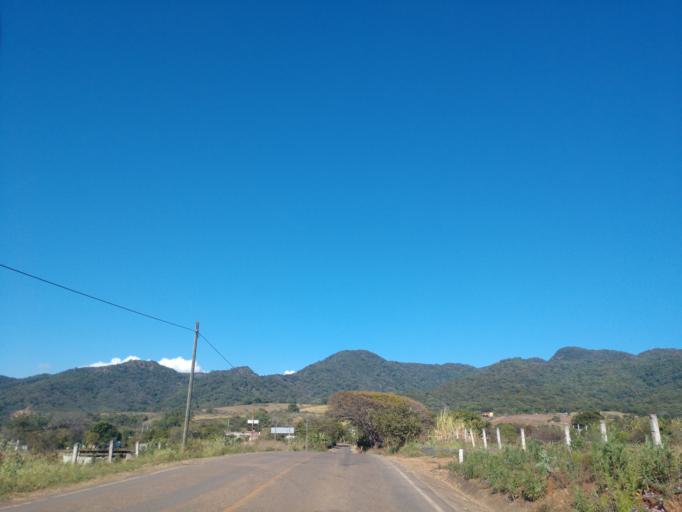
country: MX
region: Nayarit
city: Compostela
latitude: 21.2780
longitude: -104.8790
